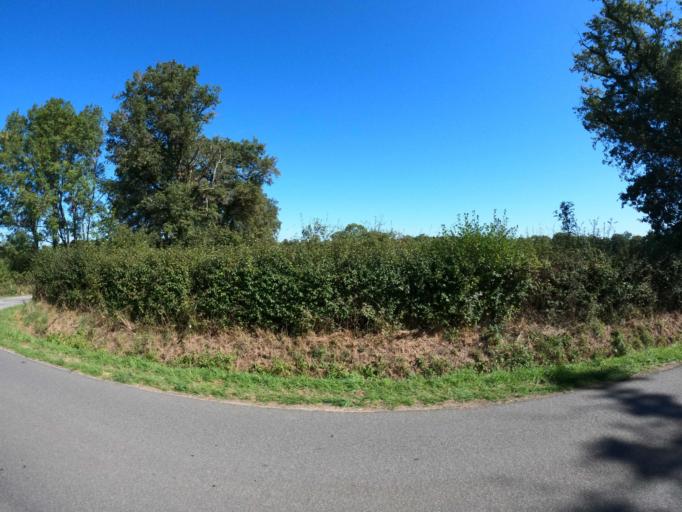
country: FR
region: Limousin
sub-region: Departement de la Haute-Vienne
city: Le Dorat
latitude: 46.2625
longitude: 1.0341
